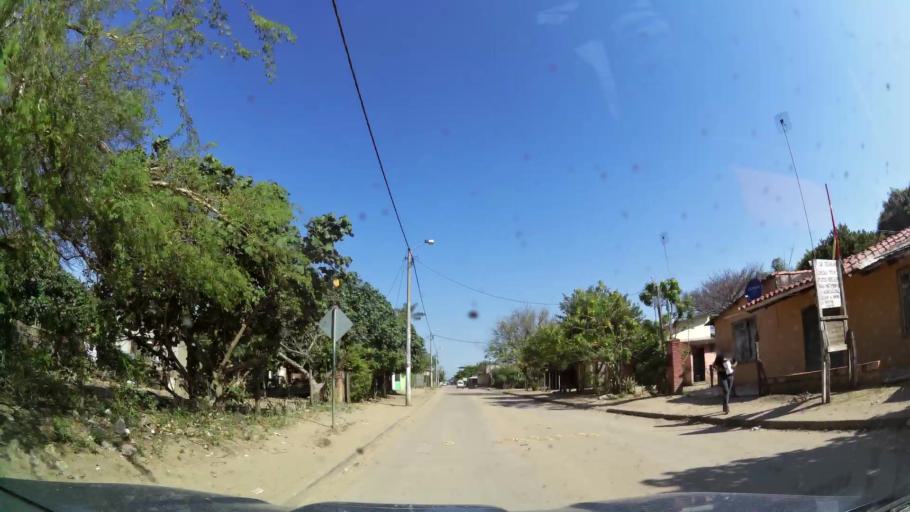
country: BO
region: Santa Cruz
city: Cotoca
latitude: -17.7363
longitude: -63.0741
